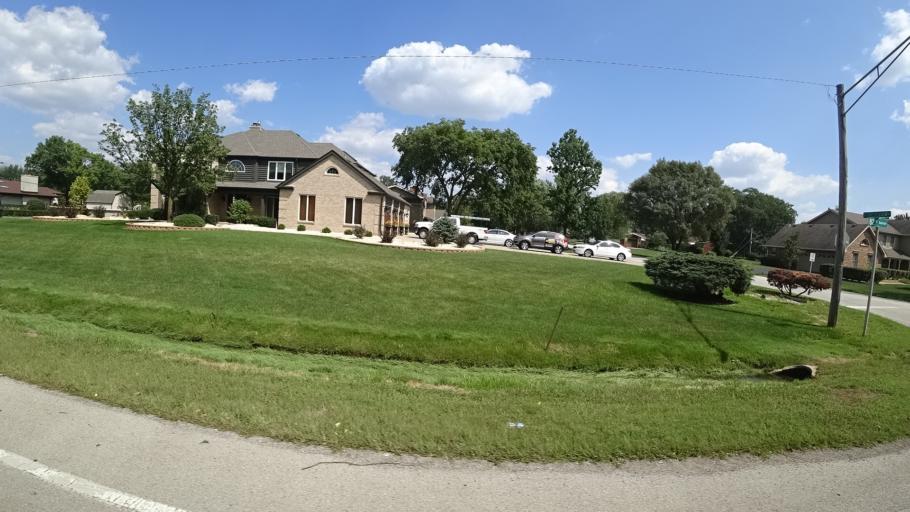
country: US
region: Illinois
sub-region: Cook County
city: Orland Park
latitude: 41.6196
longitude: -87.8192
